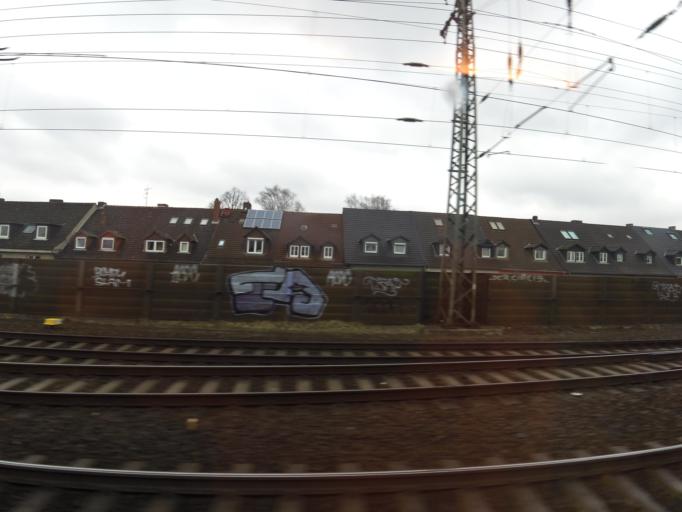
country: DE
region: Lower Saxony
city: Hannover
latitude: 52.3728
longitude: 9.7596
